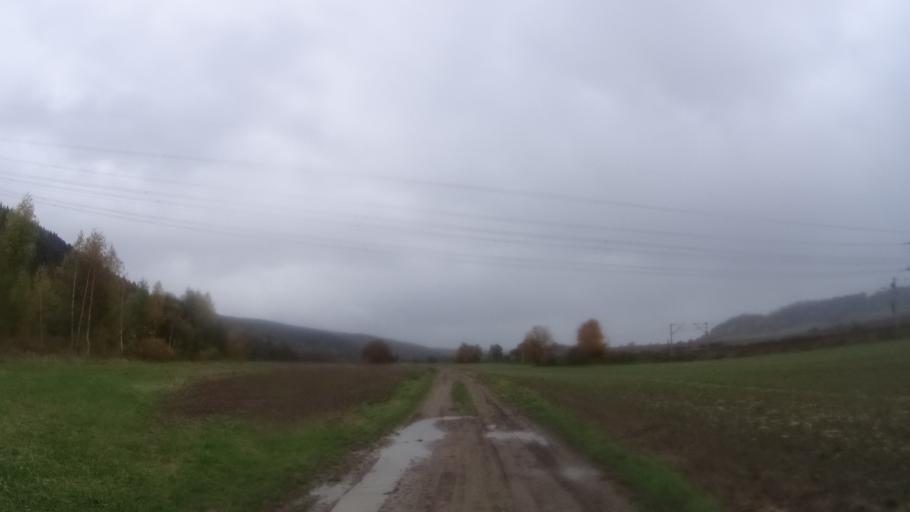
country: DE
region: Thuringia
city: Grosseutersdorf
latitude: 50.7829
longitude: 11.5634
